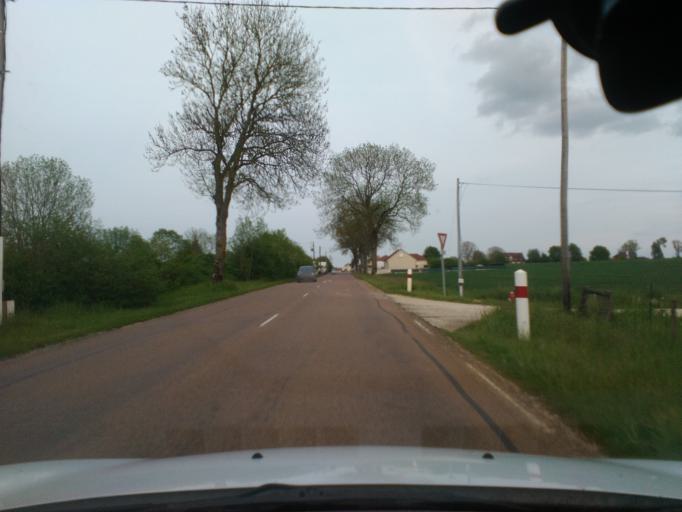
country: FR
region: Champagne-Ardenne
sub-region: Departement de la Haute-Marne
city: Chaumont
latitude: 48.1367
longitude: 5.0785
